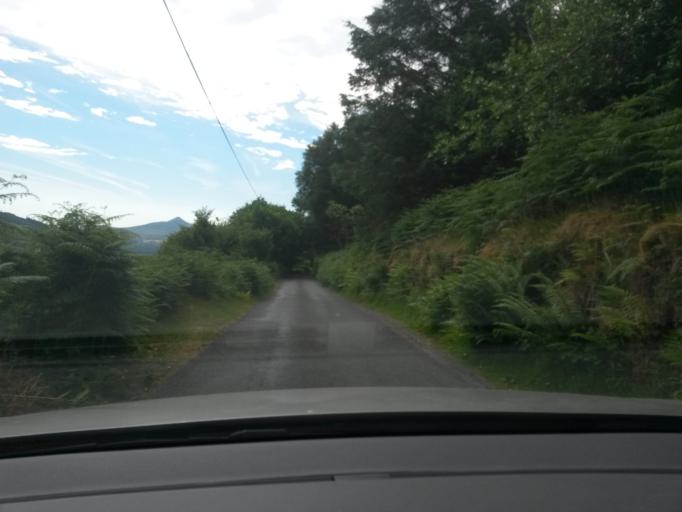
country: IE
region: Leinster
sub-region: Wicklow
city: Enniskerry
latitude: 53.1773
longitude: -6.2581
